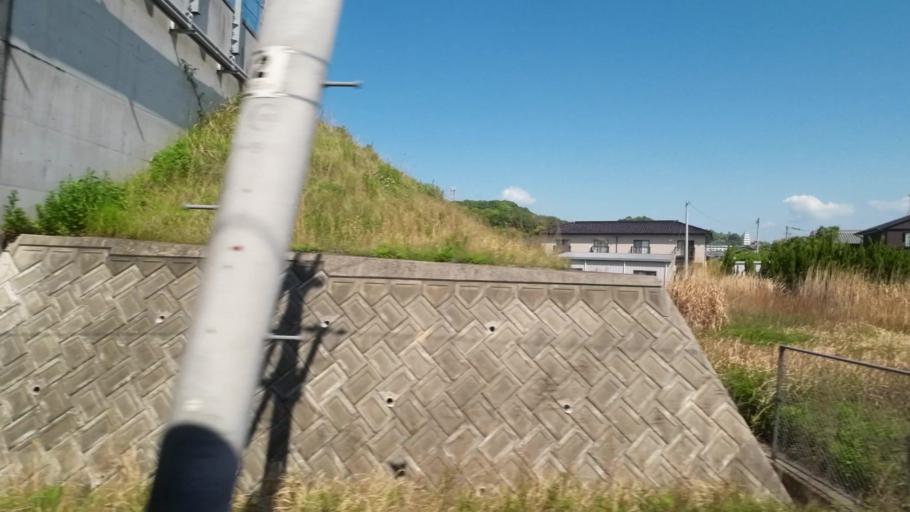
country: JP
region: Kagawa
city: Tadotsu
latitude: 34.2614
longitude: 133.7516
